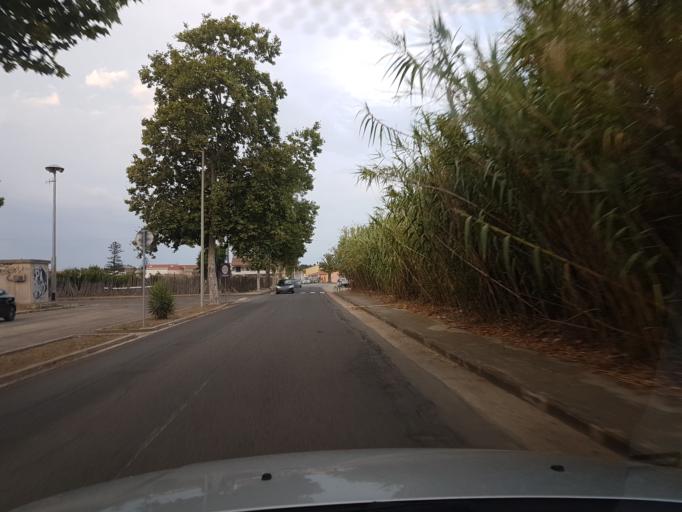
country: IT
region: Sardinia
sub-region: Provincia di Oristano
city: Solanas
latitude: 39.9303
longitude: 8.5500
